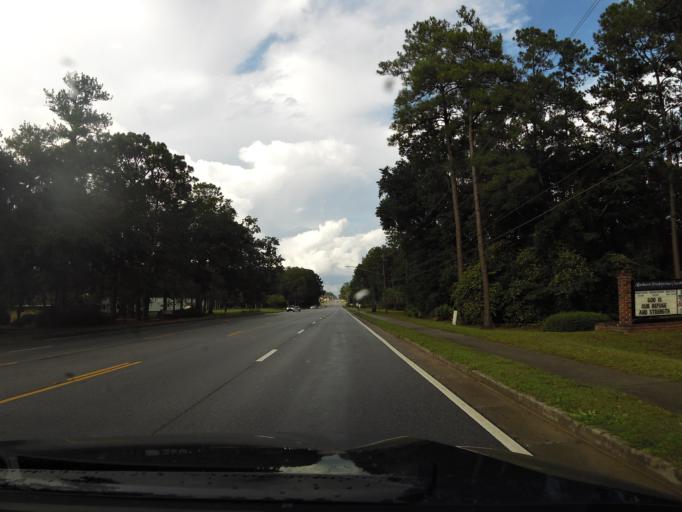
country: US
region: Georgia
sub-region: Liberty County
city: Walthourville
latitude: 31.7883
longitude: -81.6088
